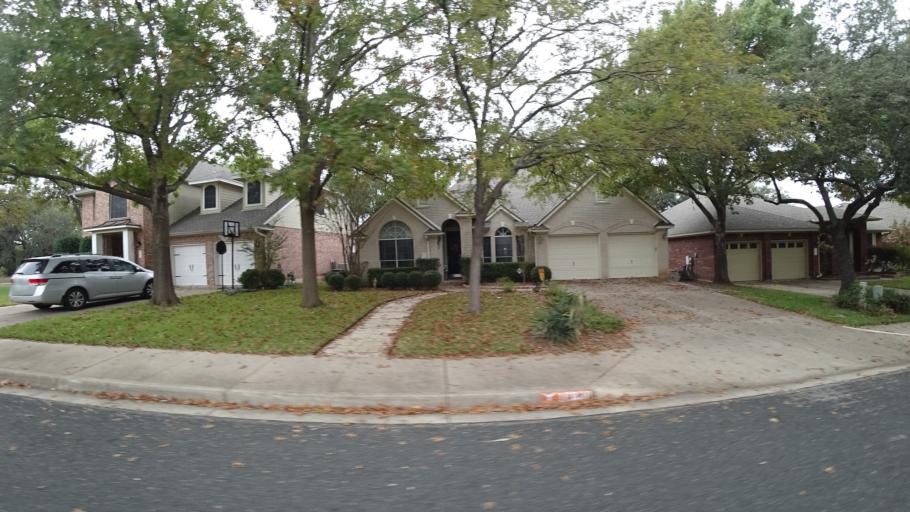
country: US
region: Texas
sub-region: Williamson County
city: Brushy Creek
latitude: 30.5114
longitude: -97.7458
